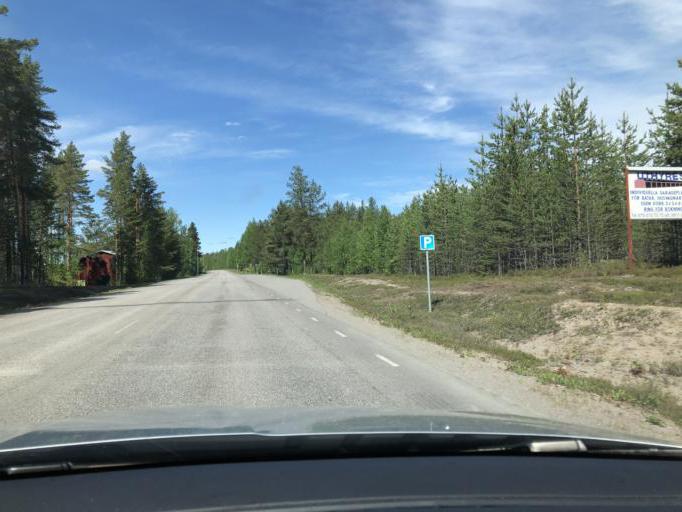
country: SE
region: Norrbotten
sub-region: Pitea Kommun
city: Bergsviken
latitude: 65.3795
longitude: 21.3418
